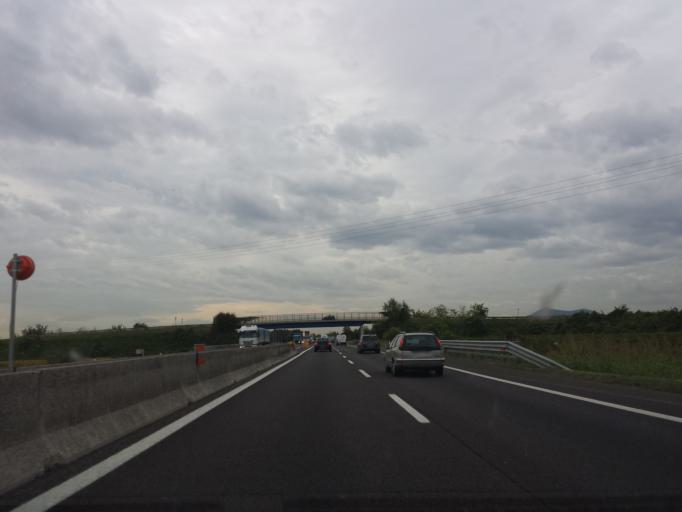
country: IT
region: Veneto
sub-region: Provincia di Padova
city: Terradura
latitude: 45.3125
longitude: 11.8240
